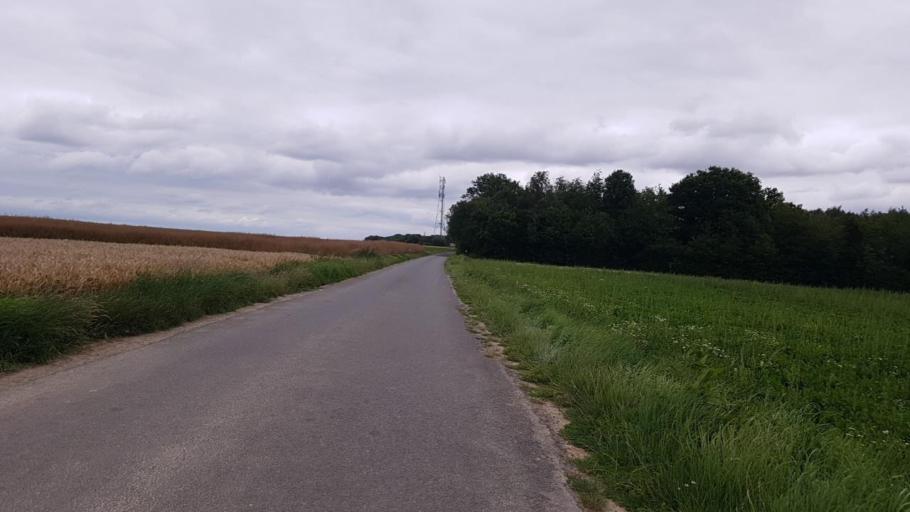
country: FR
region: Picardie
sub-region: Departement de l'Aisne
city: Guise
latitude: 49.8912
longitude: 3.5851
